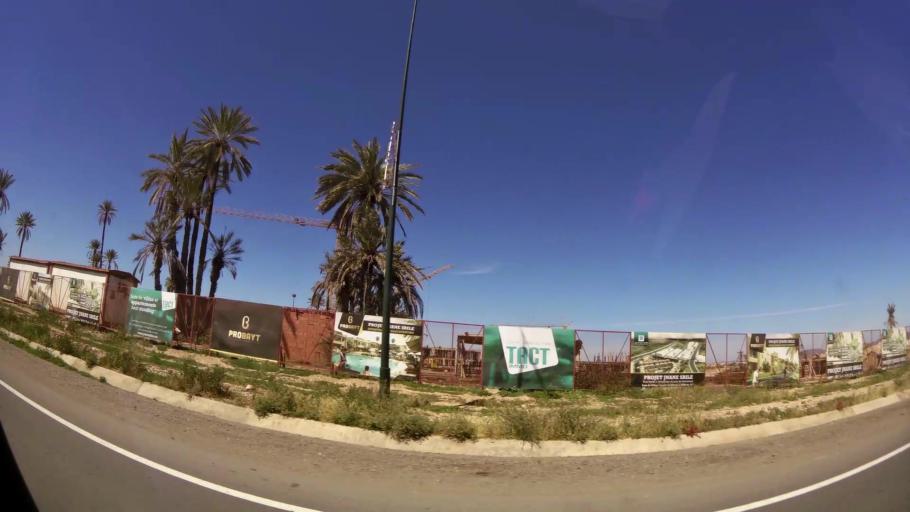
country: MA
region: Marrakech-Tensift-Al Haouz
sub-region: Marrakech
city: Marrakesh
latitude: 31.6736
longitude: -7.9904
